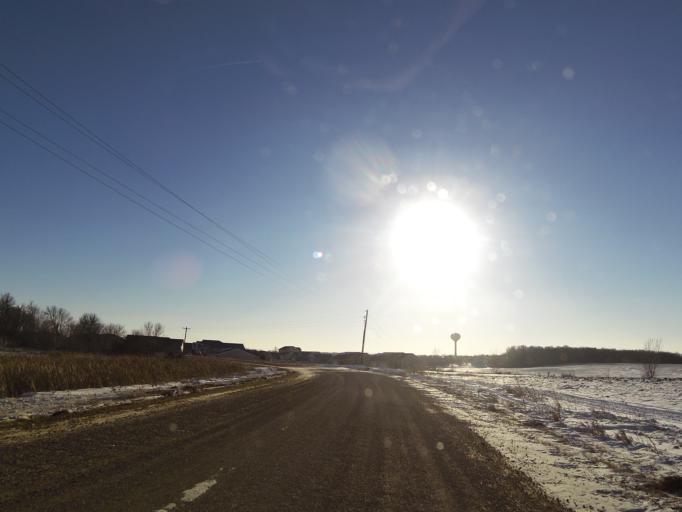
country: US
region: Minnesota
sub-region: Le Sueur County
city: New Prague
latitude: 44.5552
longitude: -93.5535
